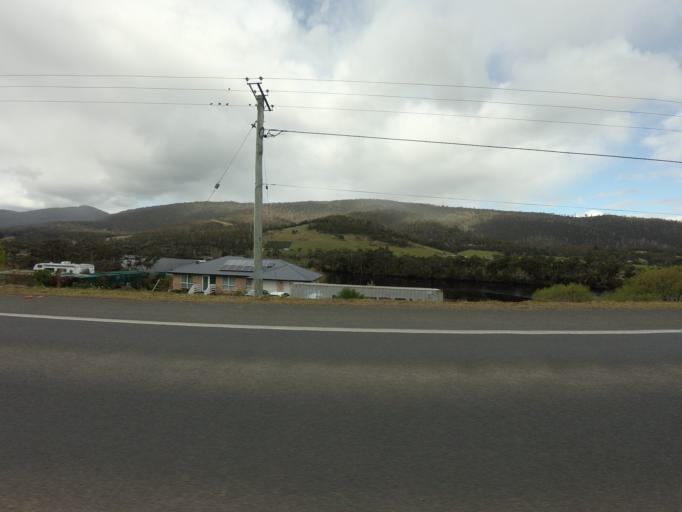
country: AU
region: Tasmania
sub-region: Huon Valley
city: Huonville
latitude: -43.0433
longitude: 147.0439
